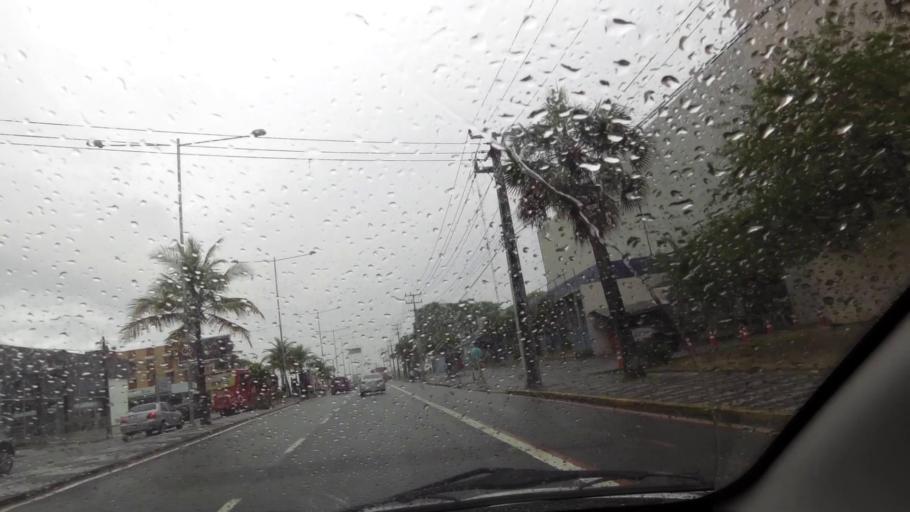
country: BR
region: Pernambuco
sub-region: Recife
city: Recife
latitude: -8.0847
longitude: -34.8873
